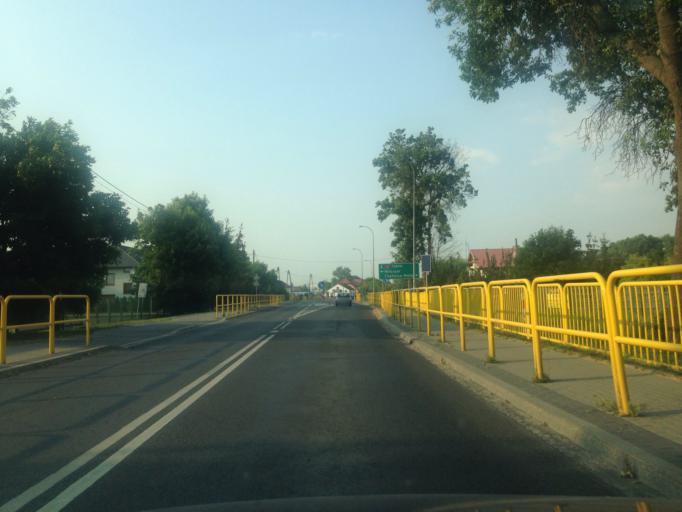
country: PL
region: Kujawsko-Pomorskie
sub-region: Powiat wloclawski
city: Fabianki
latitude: 52.7139
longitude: 19.1061
